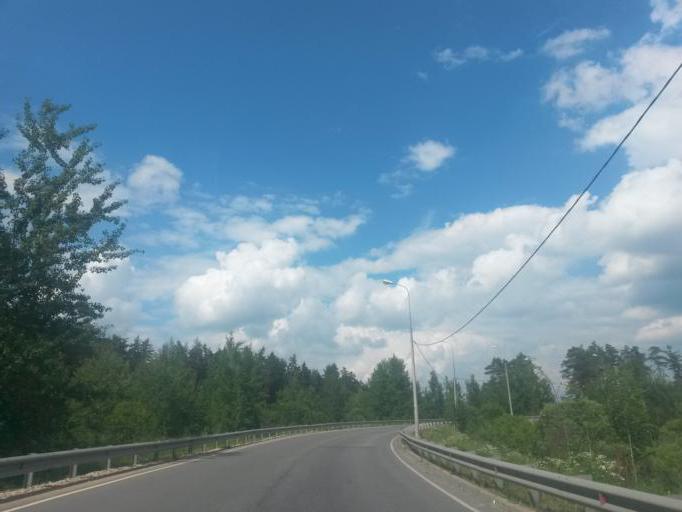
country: RU
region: Moskovskaya
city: Vostryakovo
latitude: 55.4054
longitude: 37.7824
